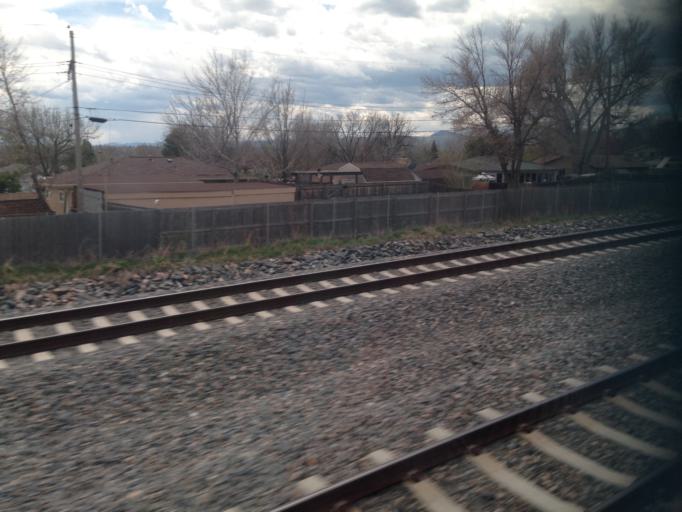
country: US
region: Colorado
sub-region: Jefferson County
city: Arvada
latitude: 39.7938
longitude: -105.1025
